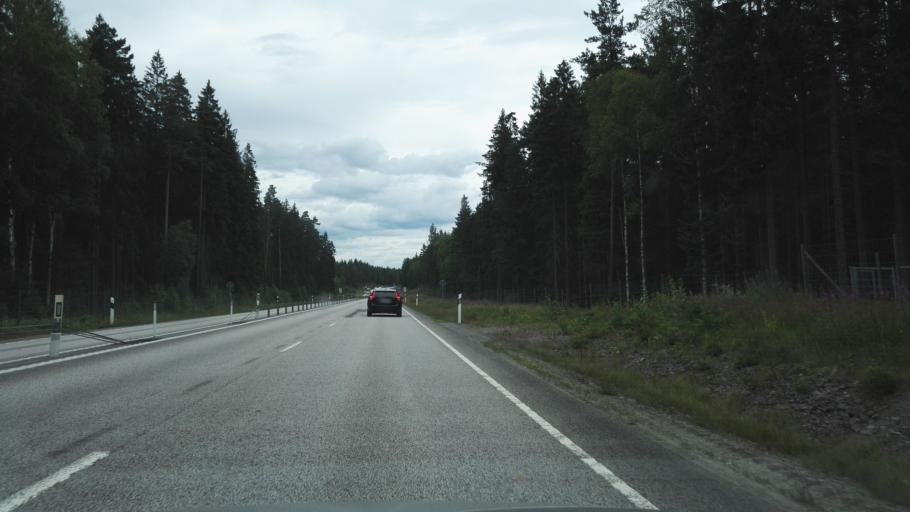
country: SE
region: Kronoberg
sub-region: Vaxjo Kommun
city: Braas
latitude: 57.0211
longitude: 15.0570
